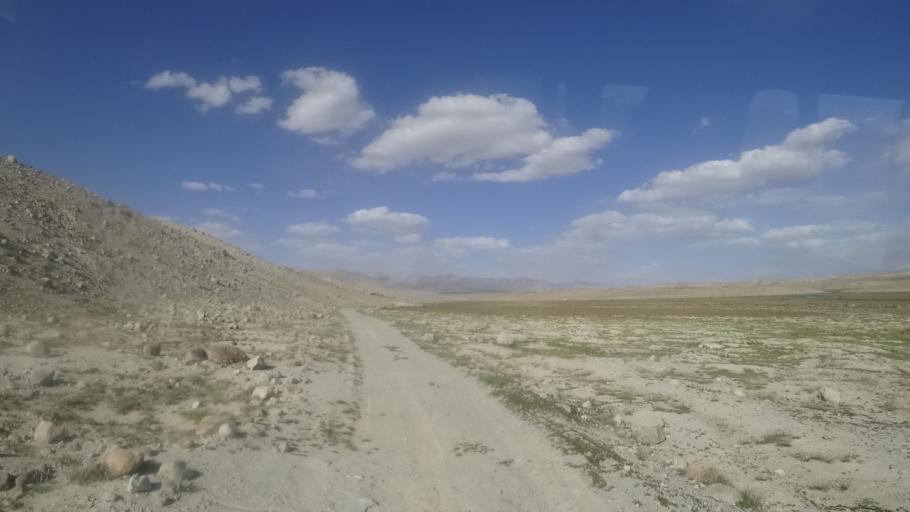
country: AF
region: Badakhshan
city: Khandud
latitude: 37.4146
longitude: 73.2263
